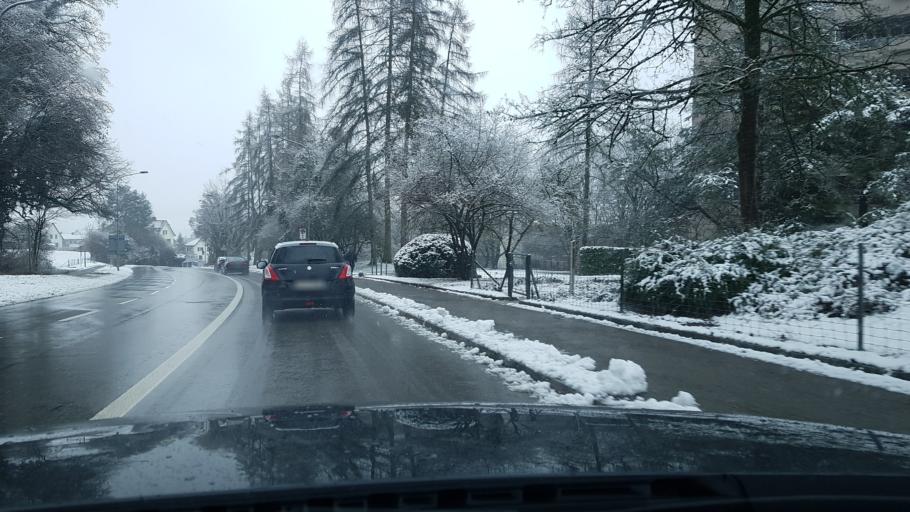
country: CH
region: Zurich
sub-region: Bezirk Zuerich
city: Zuerich (Kreis 11) / Affoltern
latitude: 47.4141
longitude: 8.5064
